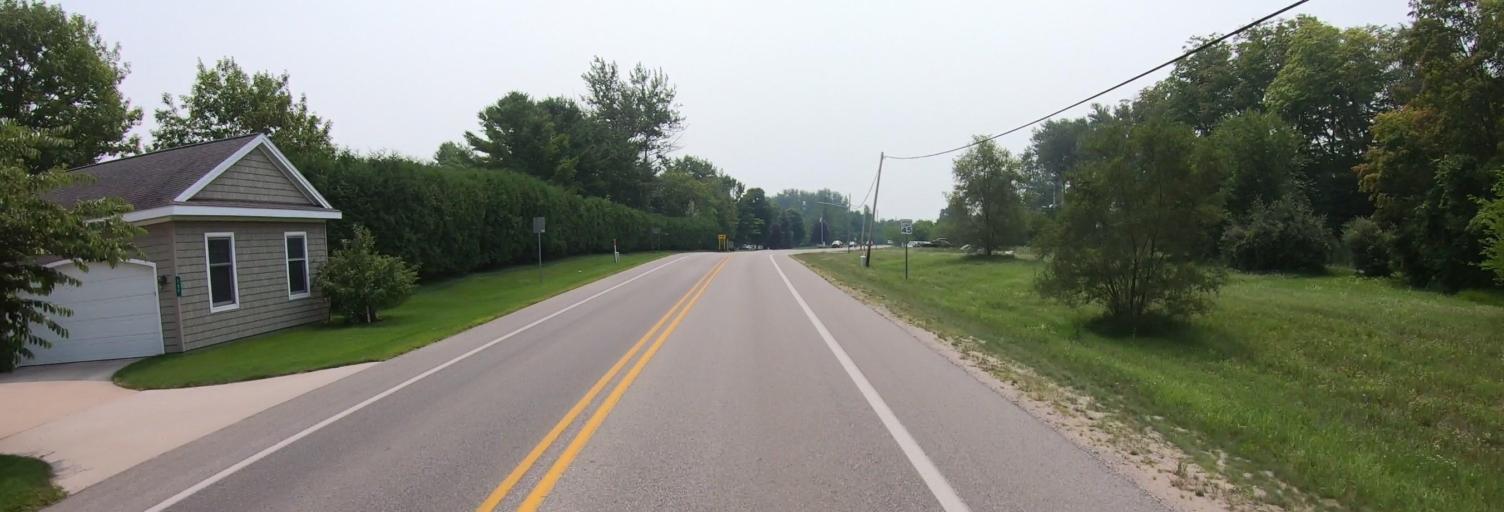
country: US
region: Michigan
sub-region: Leelanau County
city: Leland
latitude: 44.9866
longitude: -85.6416
